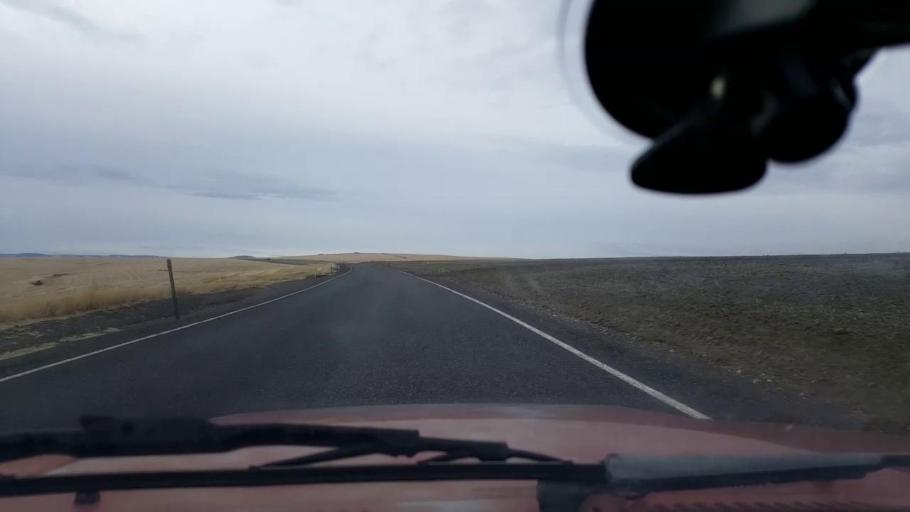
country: US
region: Washington
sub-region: Asotin County
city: Clarkston Heights-Vineland
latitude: 46.3577
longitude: -117.2179
